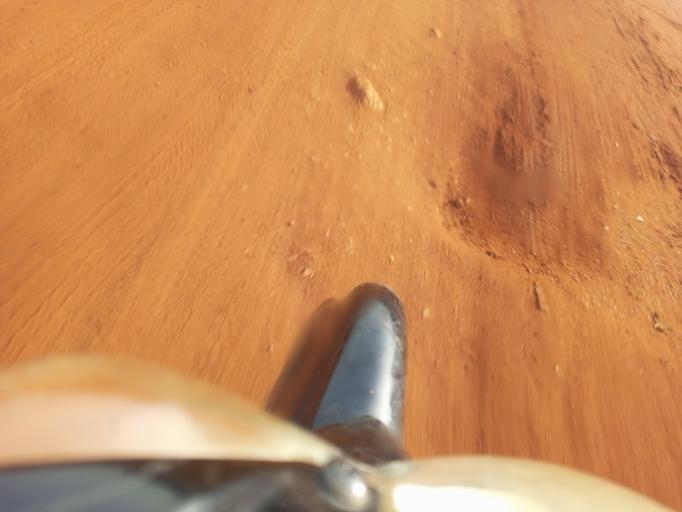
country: ML
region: Bamako
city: Bamako
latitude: 12.5321
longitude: -7.9943
